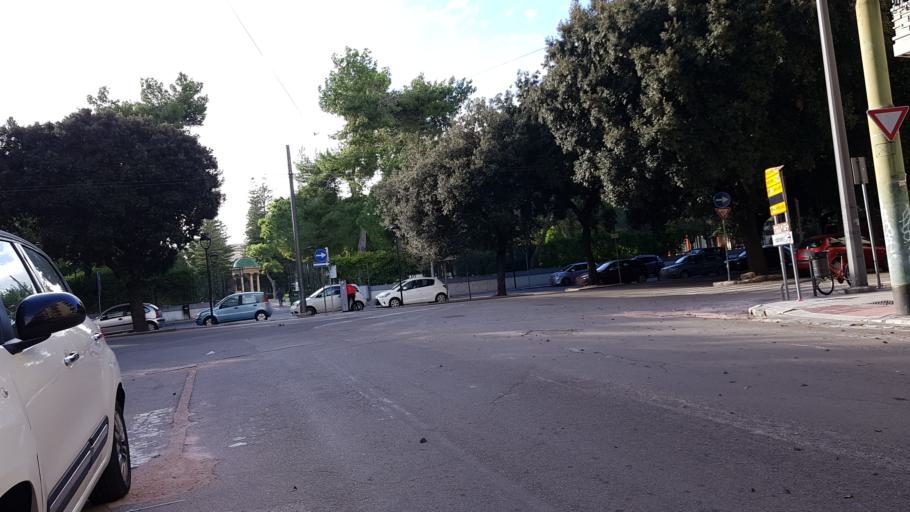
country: IT
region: Apulia
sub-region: Provincia di Lecce
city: Lecce
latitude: 40.3554
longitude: 18.1767
